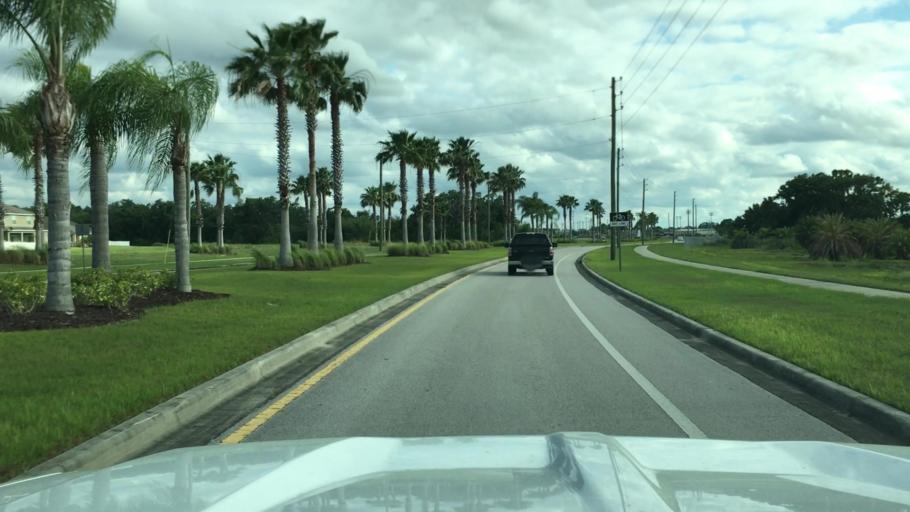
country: US
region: Florida
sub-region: Hillsborough County
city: Ruskin
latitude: 27.7324
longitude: -82.4008
